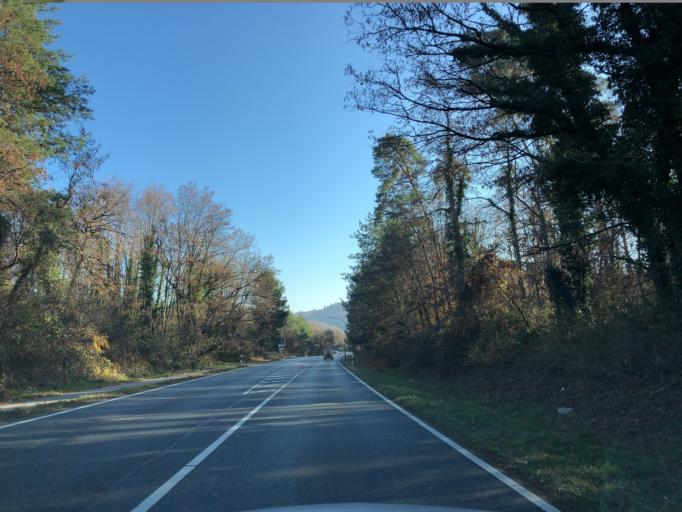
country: DE
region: Hesse
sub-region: Regierungsbezirk Darmstadt
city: Bickenbach
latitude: 49.7644
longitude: 8.6277
